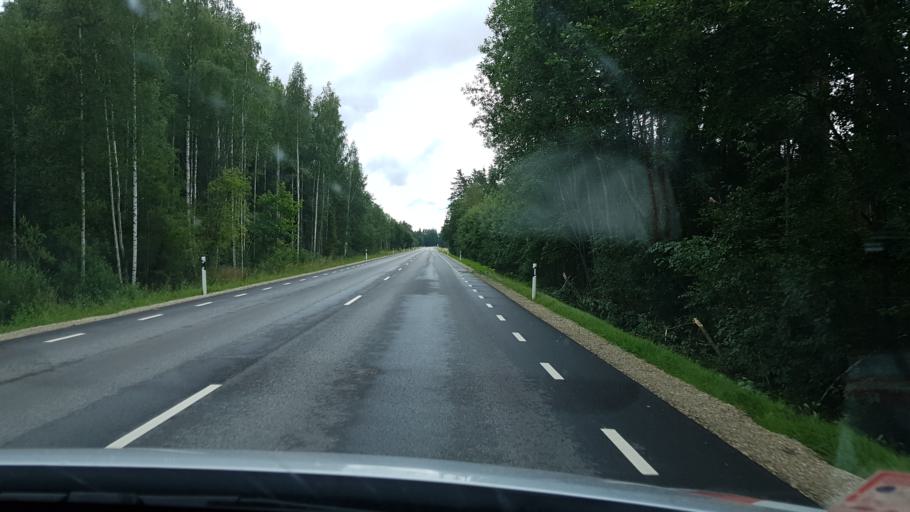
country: EE
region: Polvamaa
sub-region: Polva linn
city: Polva
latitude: 58.0414
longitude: 27.1044
